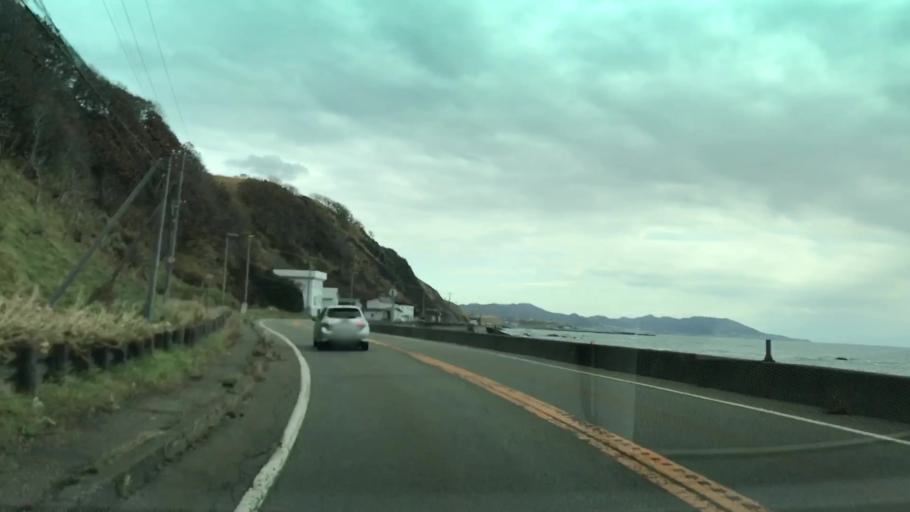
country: JP
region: Hokkaido
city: Shizunai-furukawacho
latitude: 42.0557
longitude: 143.0809
